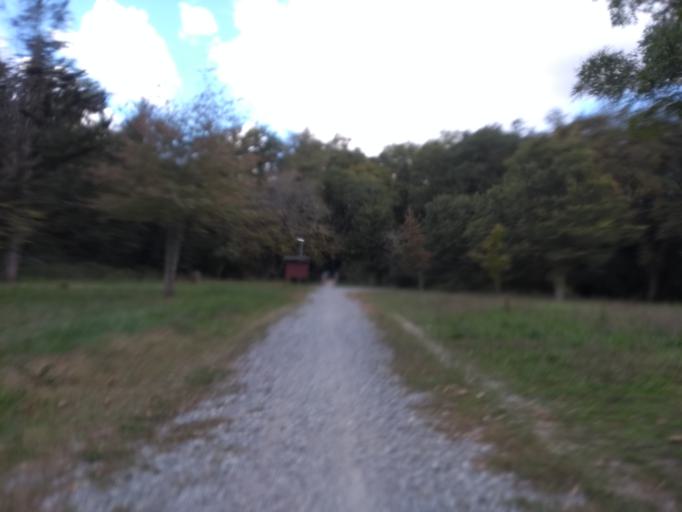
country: FR
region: Aquitaine
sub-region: Departement de la Gironde
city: Canejan
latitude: 44.7600
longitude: -0.6440
